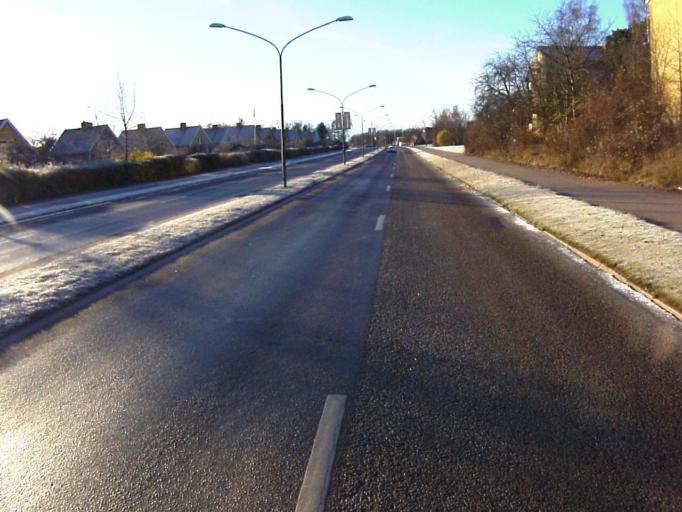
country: SE
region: Soedermanland
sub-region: Eskilstuna Kommun
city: Eskilstuna
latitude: 59.3546
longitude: 16.5003
